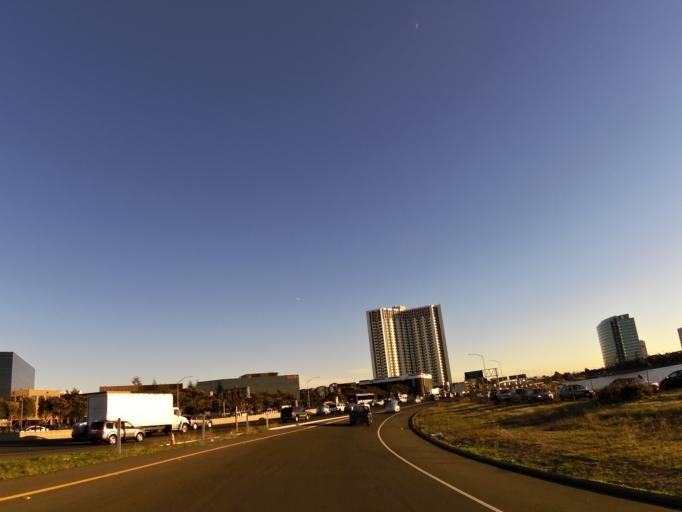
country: US
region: California
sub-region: Alameda County
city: Emeryville
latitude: 37.8462
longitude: -122.2989
